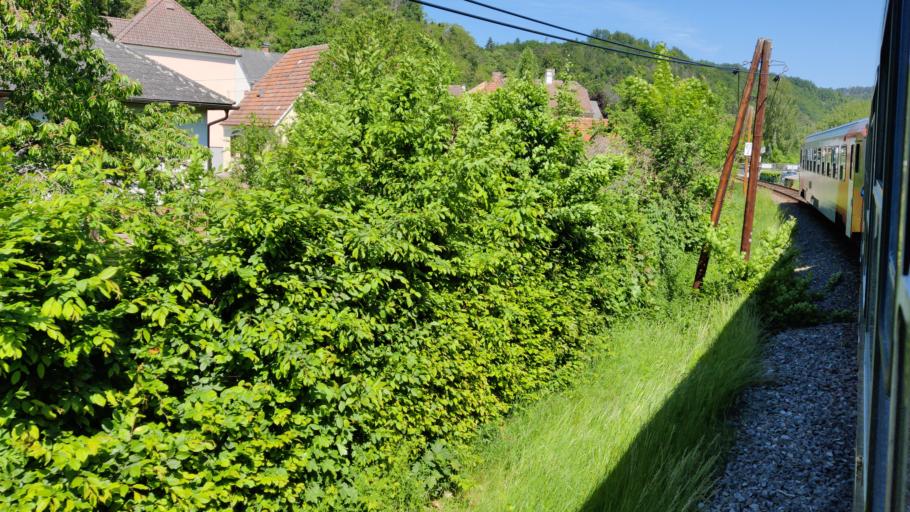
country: AT
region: Lower Austria
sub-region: Politischer Bezirk Horn
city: Gars am Kamp
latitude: 48.5936
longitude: 15.6574
